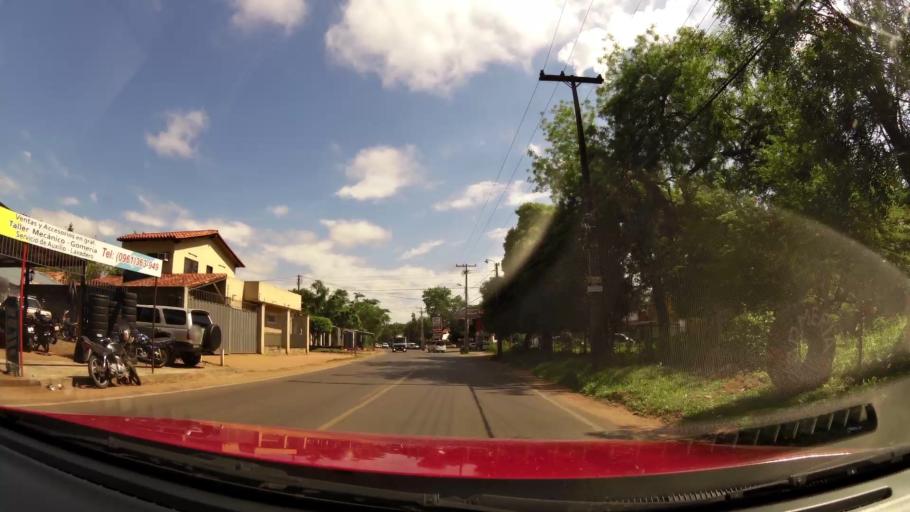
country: PY
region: Central
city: San Lorenzo
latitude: -25.2560
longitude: -57.4996
